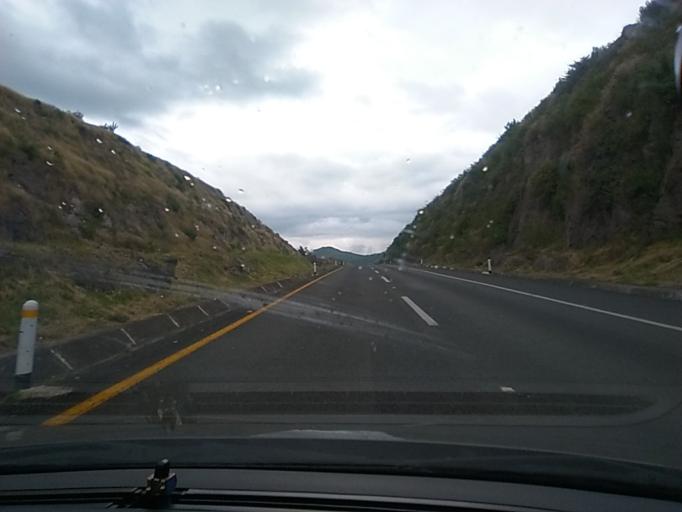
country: MX
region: Jalisco
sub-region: Zapotlanejo
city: La Mezquitera
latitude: 20.5335
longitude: -103.0143
